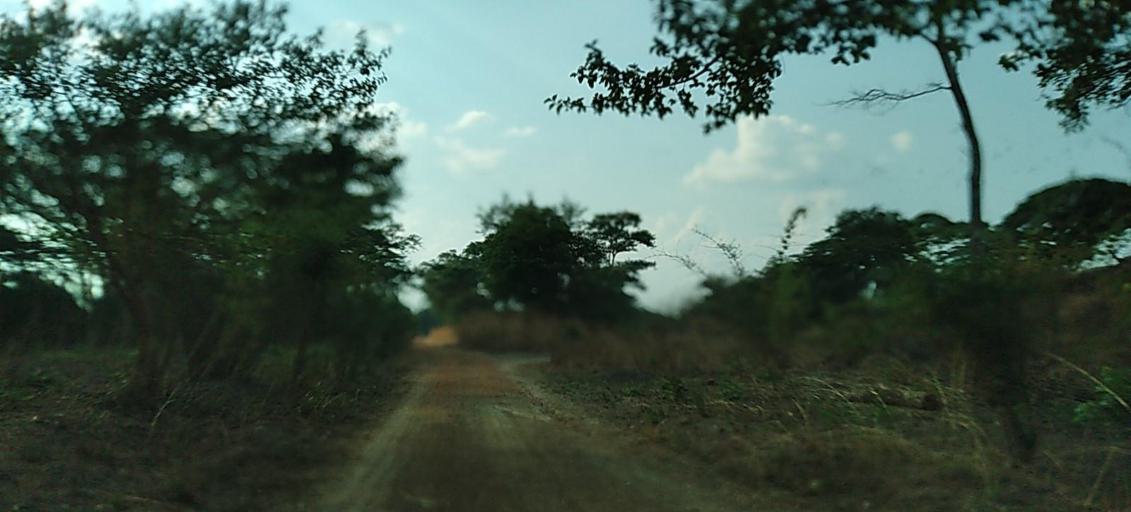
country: ZM
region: Copperbelt
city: Mpongwe
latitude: -13.4729
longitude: 28.0730
